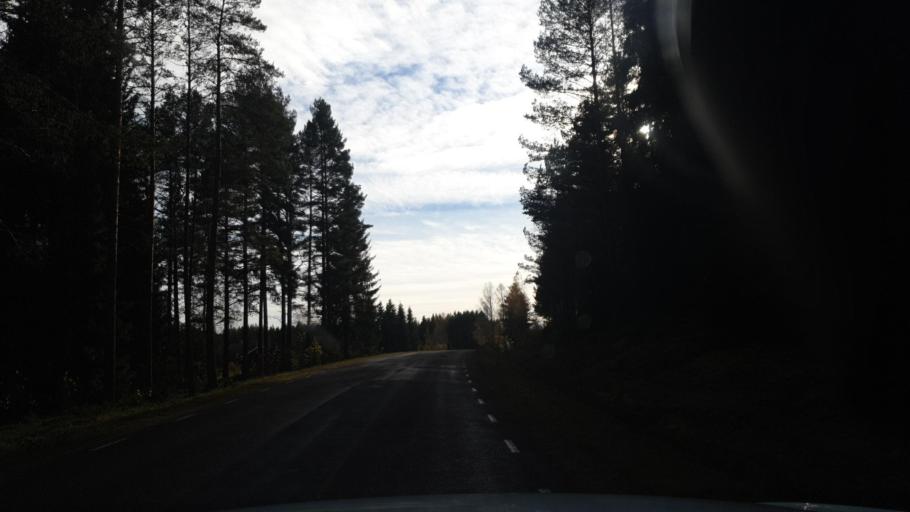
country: SE
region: Vaermland
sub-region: Eda Kommun
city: Charlottenberg
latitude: 59.9526
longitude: 12.3869
